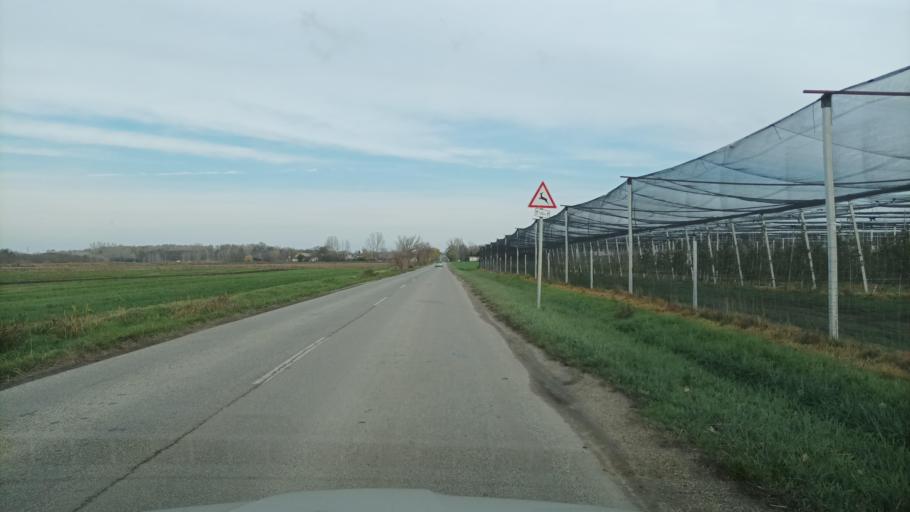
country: HU
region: Pest
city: Rackeve
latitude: 47.1142
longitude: 18.9412
